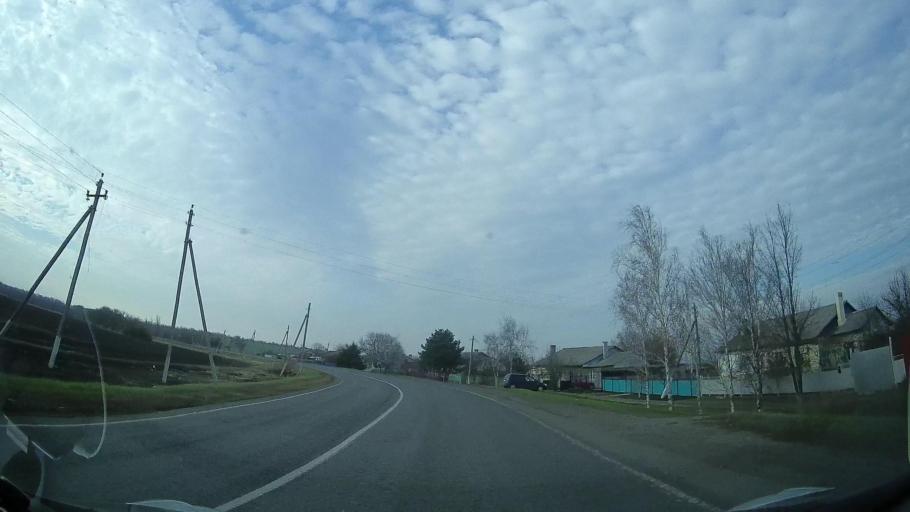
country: RU
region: Rostov
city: Bagayevskaya
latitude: 47.0953
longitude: 40.3132
